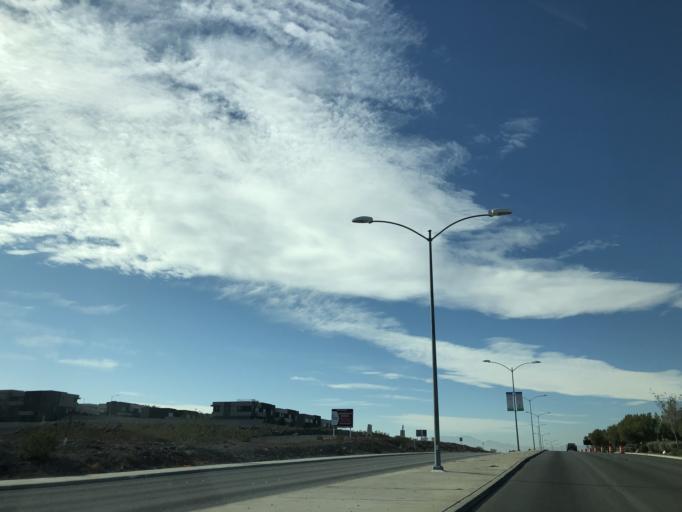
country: US
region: Nevada
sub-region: Clark County
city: Henderson
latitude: 36.0220
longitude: -115.0352
